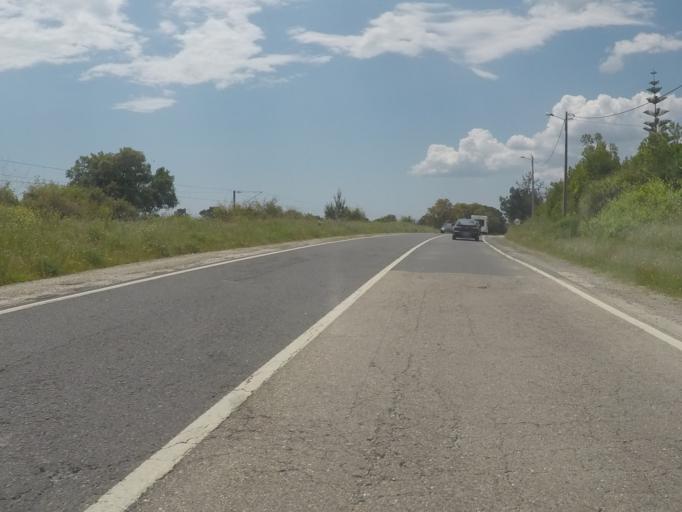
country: PT
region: Setubal
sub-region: Setubal
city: Setubal
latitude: 38.5577
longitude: -8.7942
